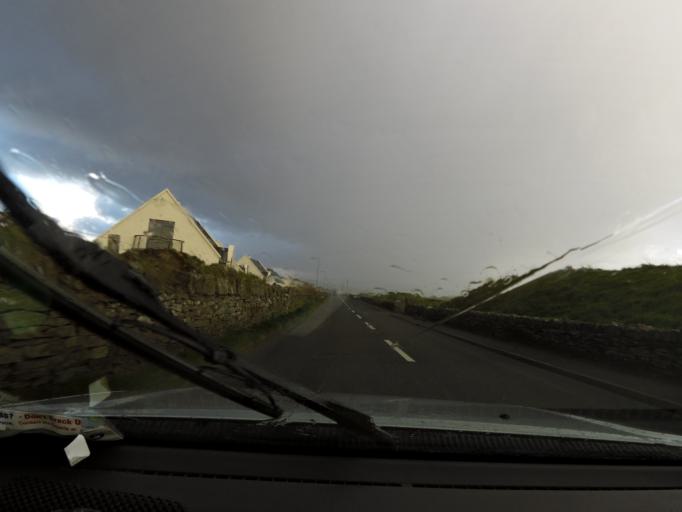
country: IE
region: Munster
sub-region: An Clar
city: Kilrush
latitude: 52.9435
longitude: -9.3499
